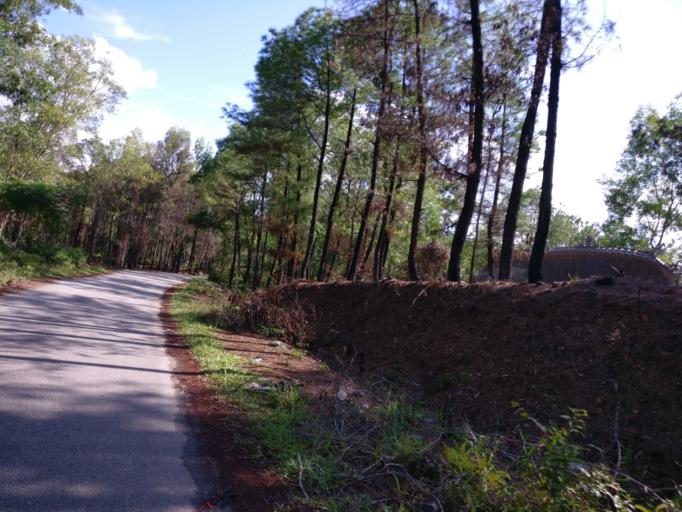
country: VN
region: Thua Thien-Hue
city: Hue
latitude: 16.4089
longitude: 107.5936
